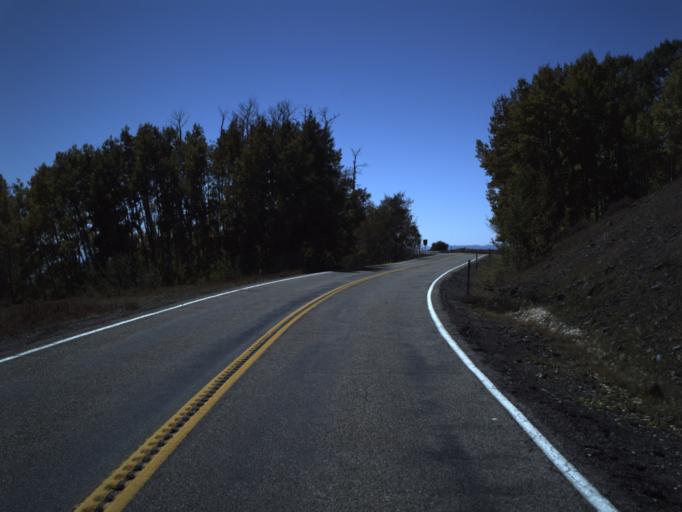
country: US
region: Utah
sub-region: Wayne County
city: Loa
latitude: 38.0295
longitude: -111.3424
